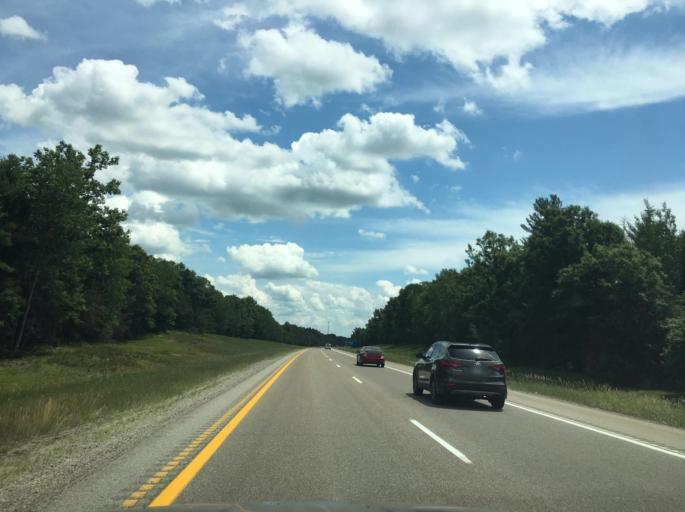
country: US
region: Michigan
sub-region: Roscommon County
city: Roscommon
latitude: 44.5335
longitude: -84.6824
